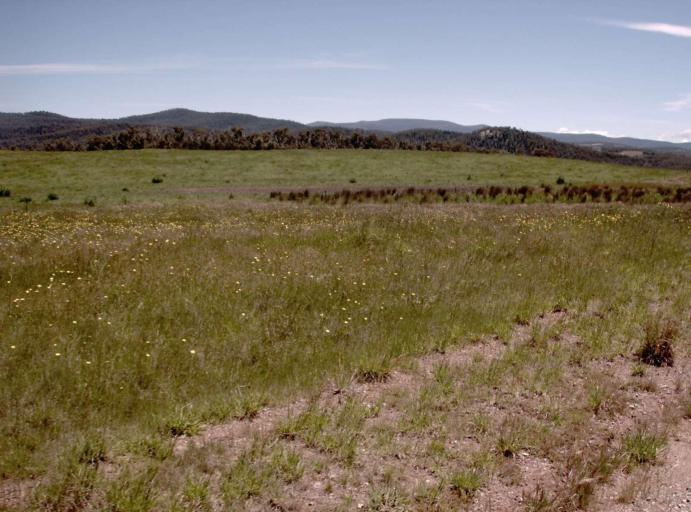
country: AU
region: New South Wales
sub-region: Snowy River
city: Jindabyne
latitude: -37.0860
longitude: 148.2580
